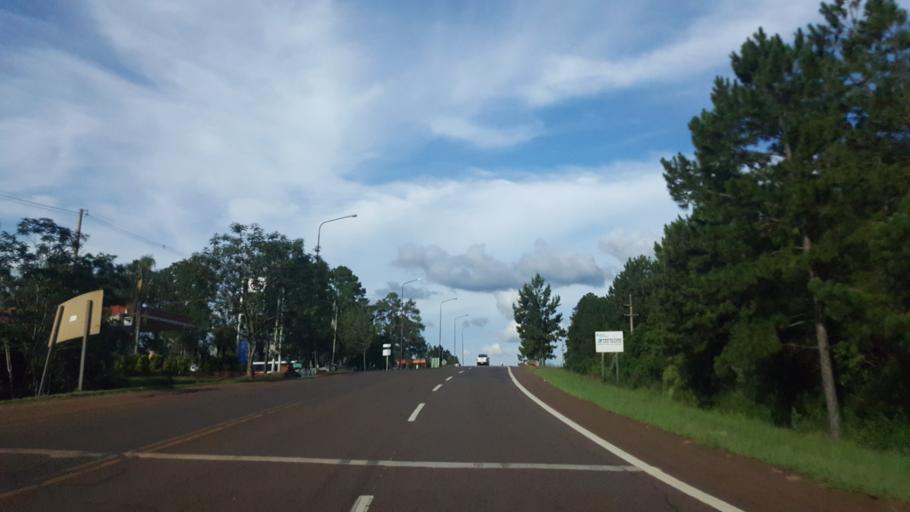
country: AR
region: Misiones
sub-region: Departamento de San Ignacio
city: San Ignacio
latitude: -27.2683
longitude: -55.5396
